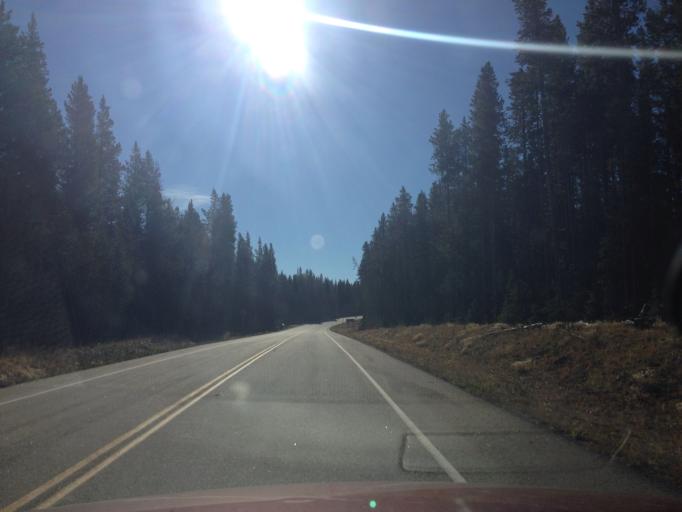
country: US
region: Montana
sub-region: Carbon County
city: Red Lodge
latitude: 45.0231
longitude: -109.8784
